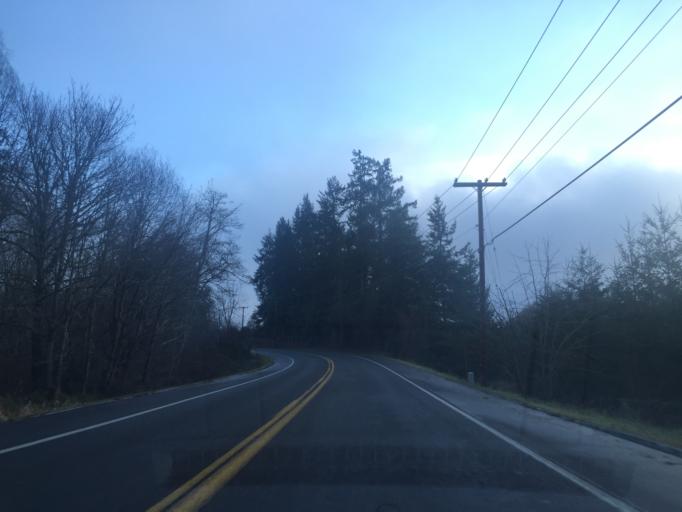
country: US
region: Washington
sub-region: Thurston County
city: Olympia
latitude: 47.1193
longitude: -122.8839
